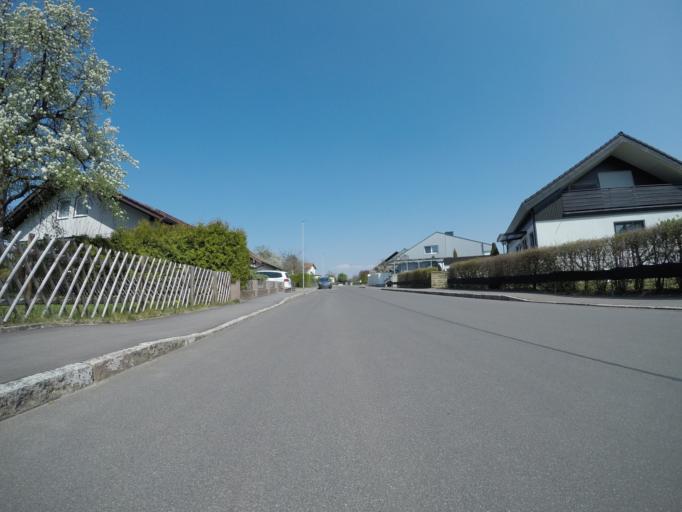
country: DE
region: Baden-Wuerttemberg
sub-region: Tuebingen Region
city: Wannweil
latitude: 48.4751
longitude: 9.1444
